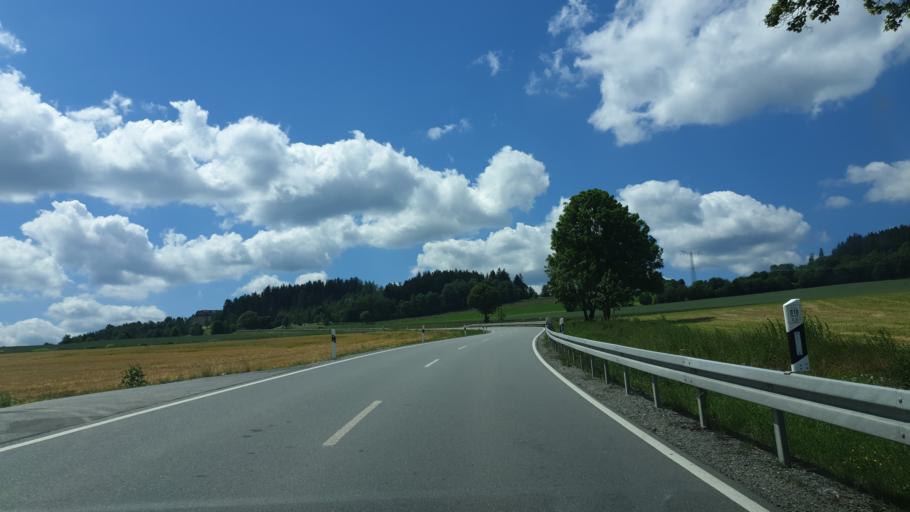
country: DE
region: Saxony
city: Schwarzenberg
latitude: 50.5287
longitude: 12.7691
